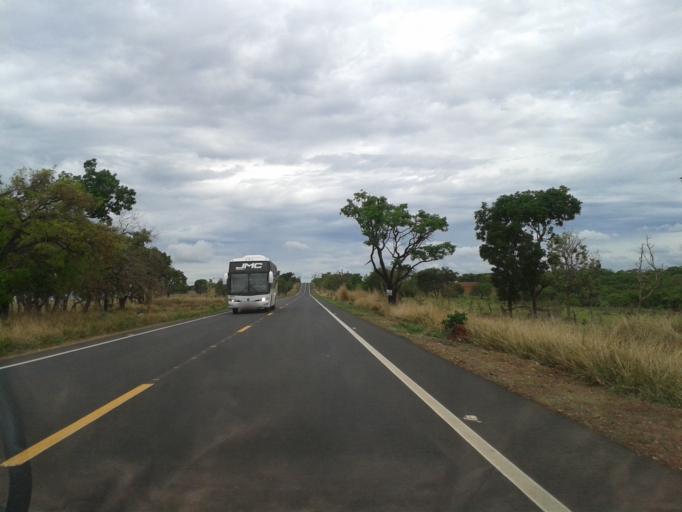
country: BR
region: Goias
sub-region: Caldas Novas
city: Caldas Novas
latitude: -17.8681
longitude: -48.6437
